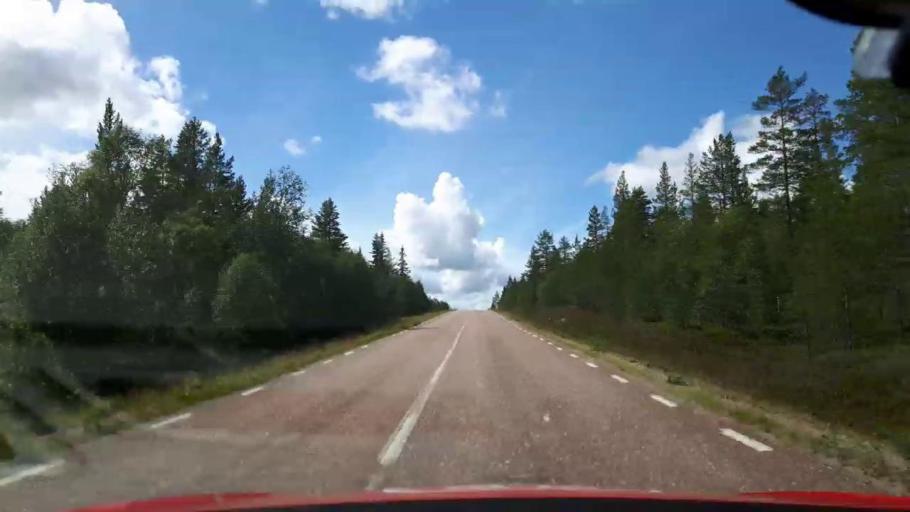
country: SE
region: Dalarna
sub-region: Alvdalens Kommun
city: AElvdalen
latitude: 61.8148
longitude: 13.5395
